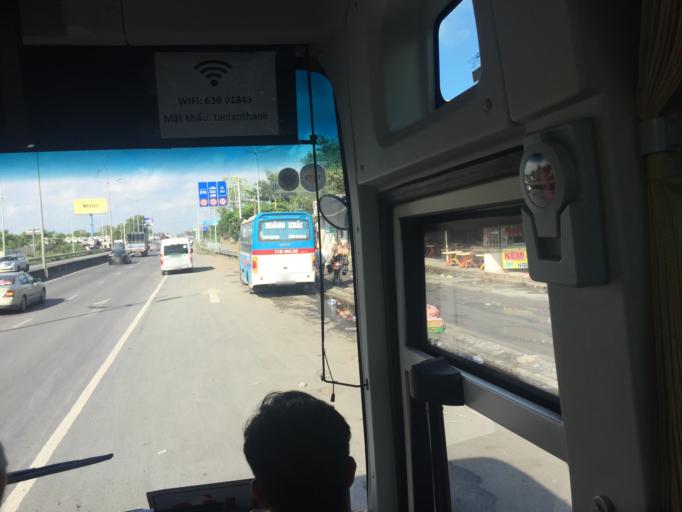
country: VN
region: Ho Chi Minh City
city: Tan Tuc
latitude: 10.6862
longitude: 106.5754
